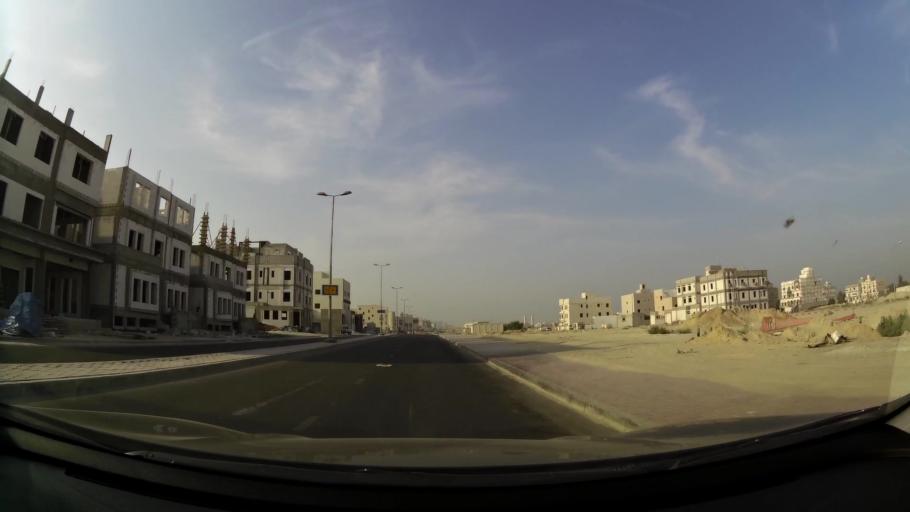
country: KW
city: Al Funaytis
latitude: 29.2222
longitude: 48.0923
